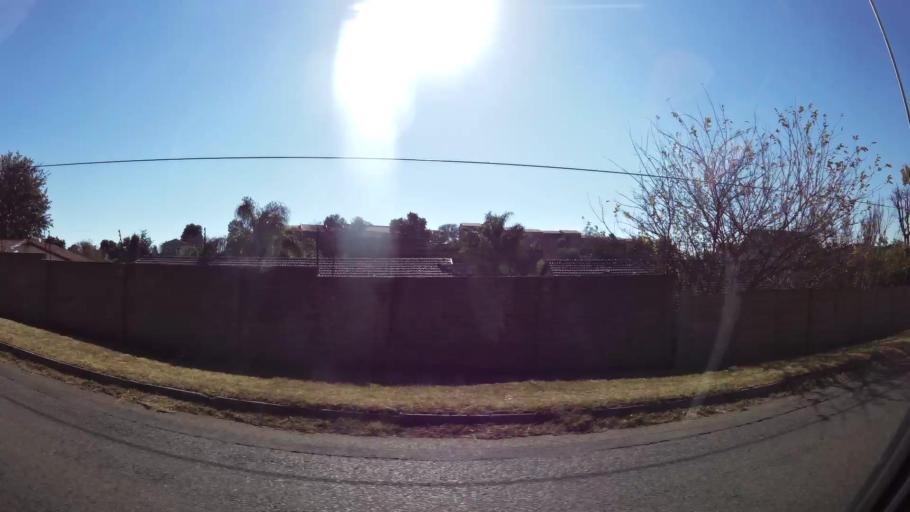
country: ZA
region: Gauteng
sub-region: City of Johannesburg Metropolitan Municipality
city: Roodepoort
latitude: -26.1181
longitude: 27.8550
